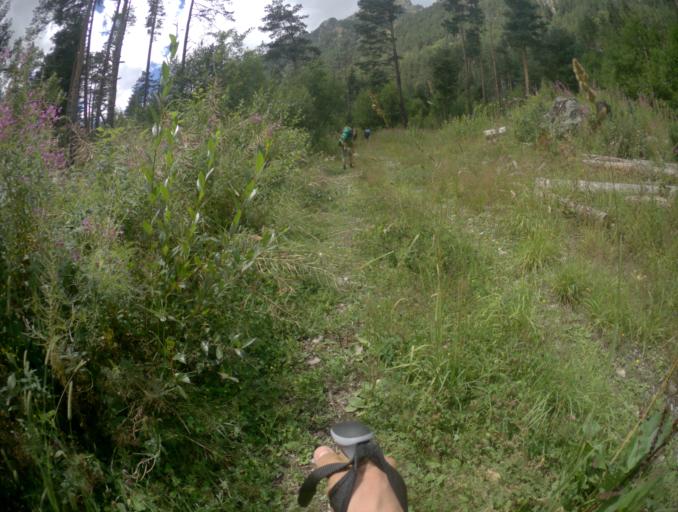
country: RU
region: Karachayevo-Cherkesiya
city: Uchkulan
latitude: 43.3540
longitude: 42.1661
